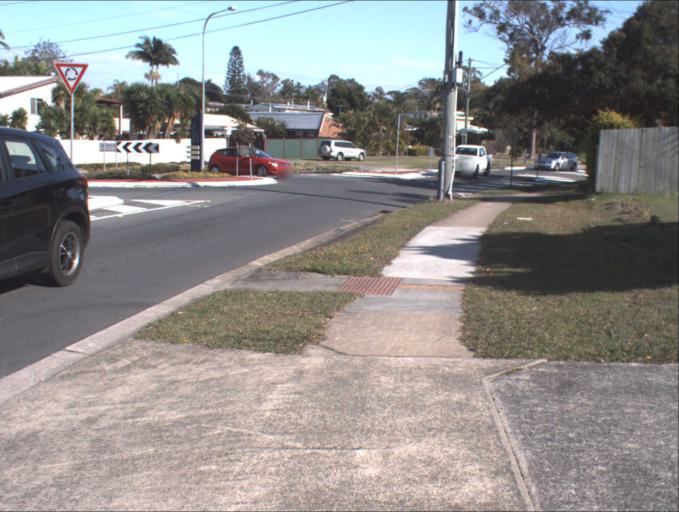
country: AU
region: Queensland
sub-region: Logan
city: Logan Reserve
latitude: -27.6869
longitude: 153.0951
